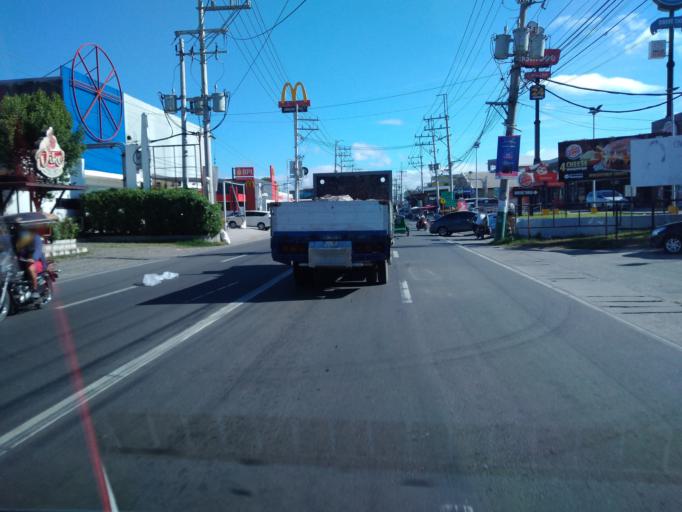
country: PH
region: Central Luzon
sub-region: Province of Bulacan
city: Santa Maria
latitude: 14.8210
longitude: 120.9521
